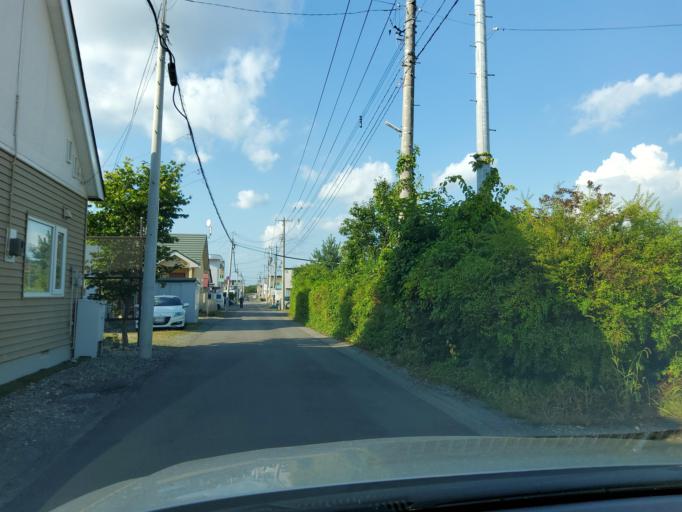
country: JP
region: Hokkaido
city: Obihiro
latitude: 42.8920
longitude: 143.1979
